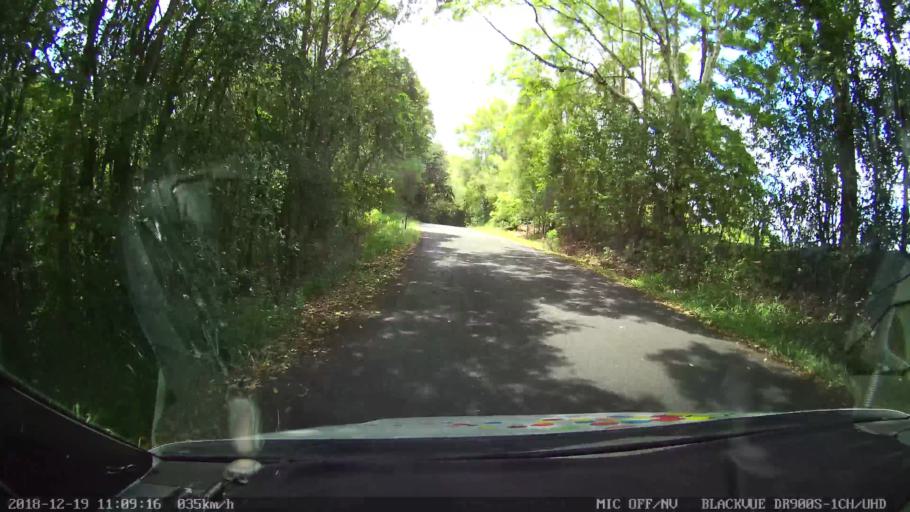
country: AU
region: New South Wales
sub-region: Lismore Municipality
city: Nimbin
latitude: -28.6337
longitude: 153.2640
